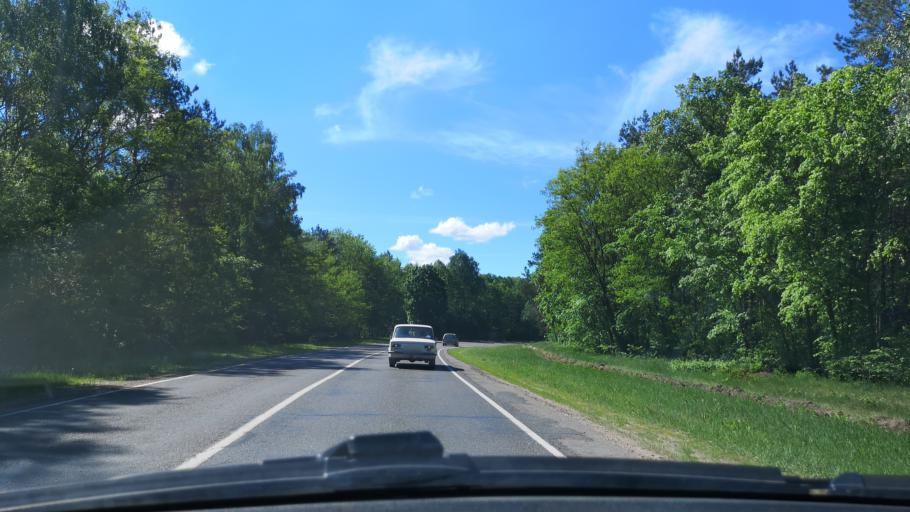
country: BY
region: Brest
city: Brest
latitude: 52.0229
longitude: 23.7302
